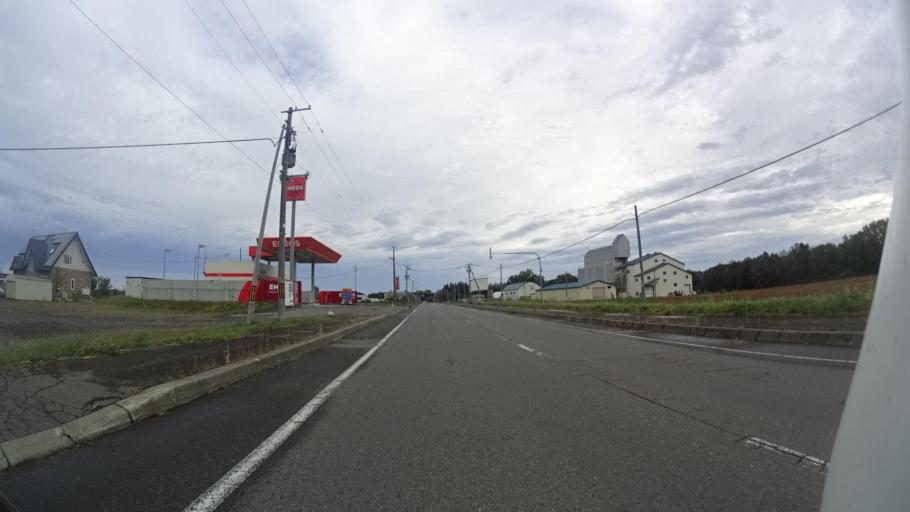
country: JP
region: Hokkaido
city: Abashiri
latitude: 43.8452
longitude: 144.5973
